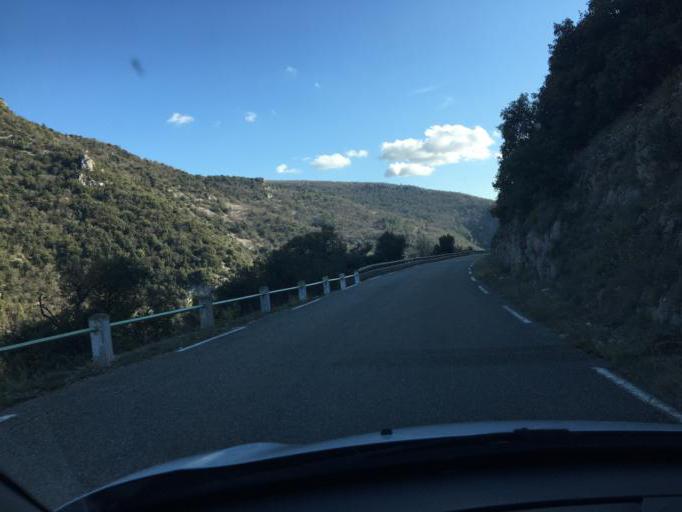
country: FR
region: Provence-Alpes-Cote d'Azur
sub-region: Departement du Vaucluse
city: Villes-sur-Auzon
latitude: 44.0612
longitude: 5.3018
